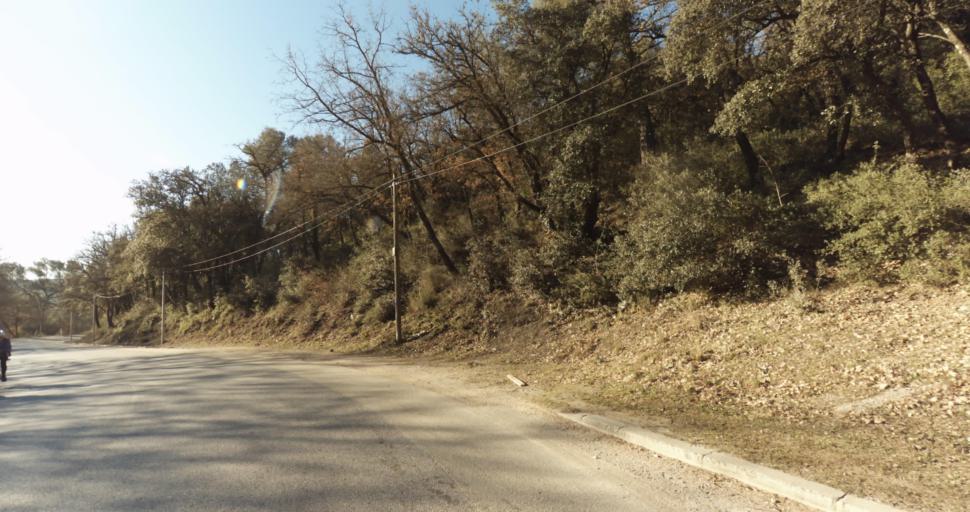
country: FR
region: Provence-Alpes-Cote d'Azur
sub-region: Departement des Bouches-du-Rhone
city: Cadolive
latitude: 43.4052
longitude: 5.5663
